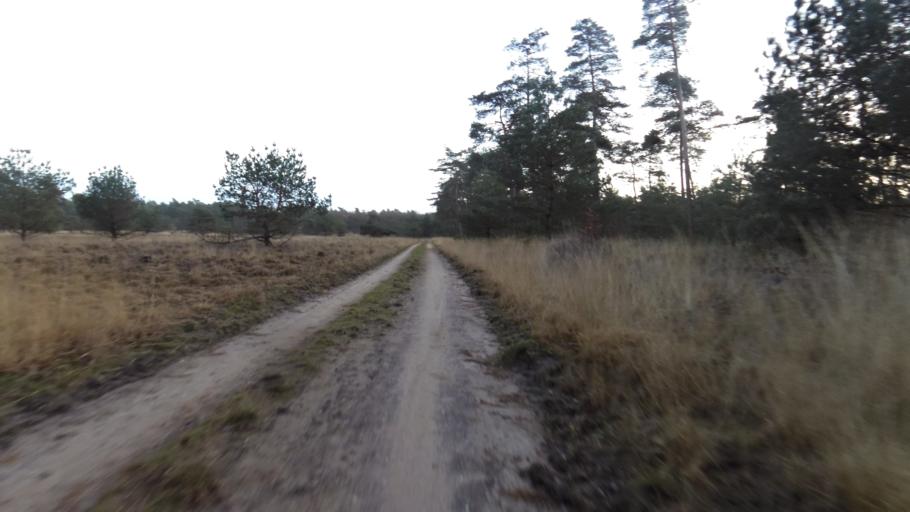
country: NL
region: Gelderland
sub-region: Gemeente Apeldoorn
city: Uddel
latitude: 52.2906
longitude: 5.8512
